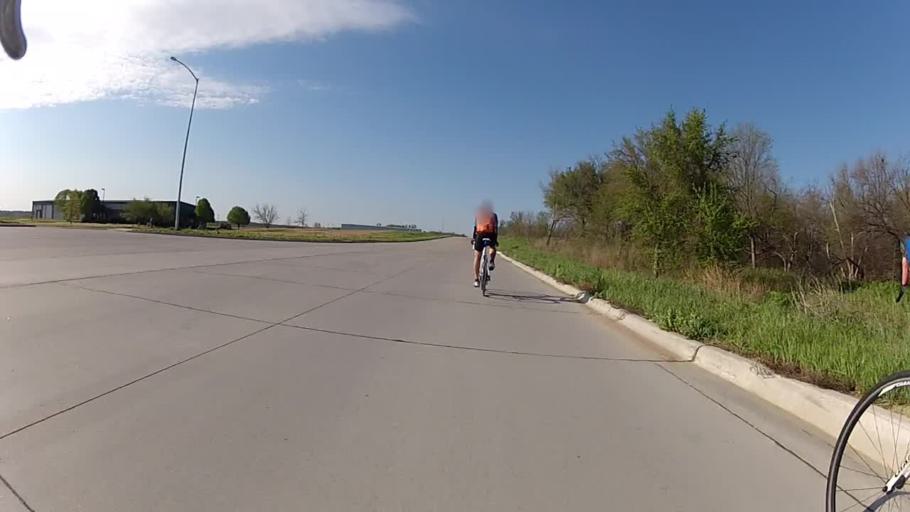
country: US
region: Kansas
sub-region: Riley County
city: Ogden
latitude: 39.1448
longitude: -96.6820
